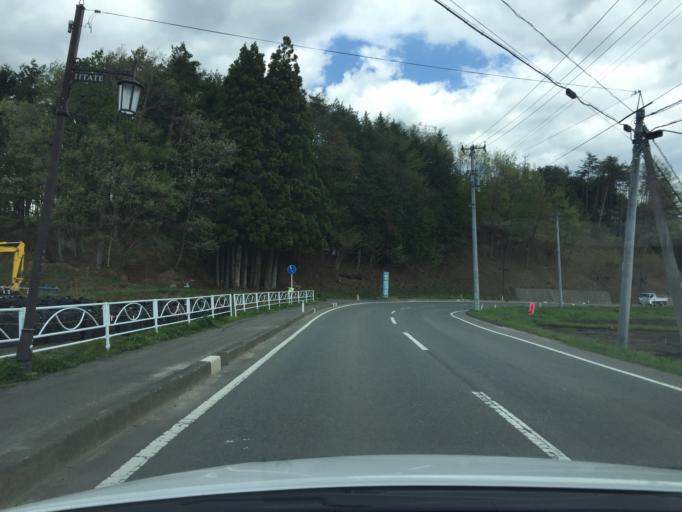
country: JP
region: Fukushima
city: Yanagawamachi-saiwaicho
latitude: 37.6899
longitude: 140.7431
